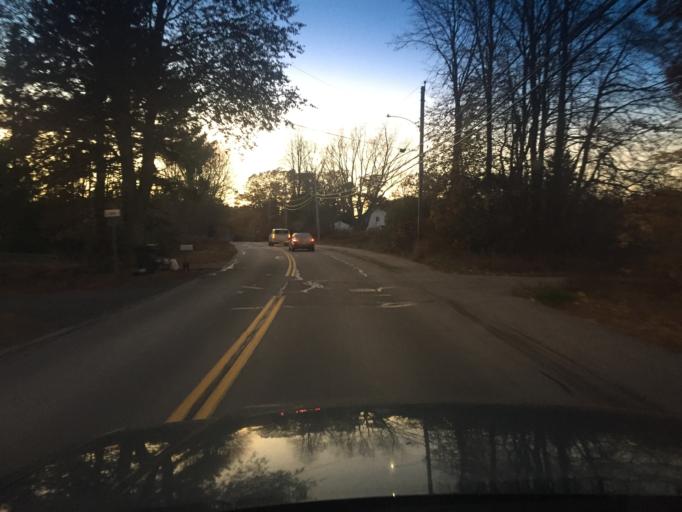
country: US
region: Maine
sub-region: York County
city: York Harbor
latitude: 43.1492
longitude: -70.6370
